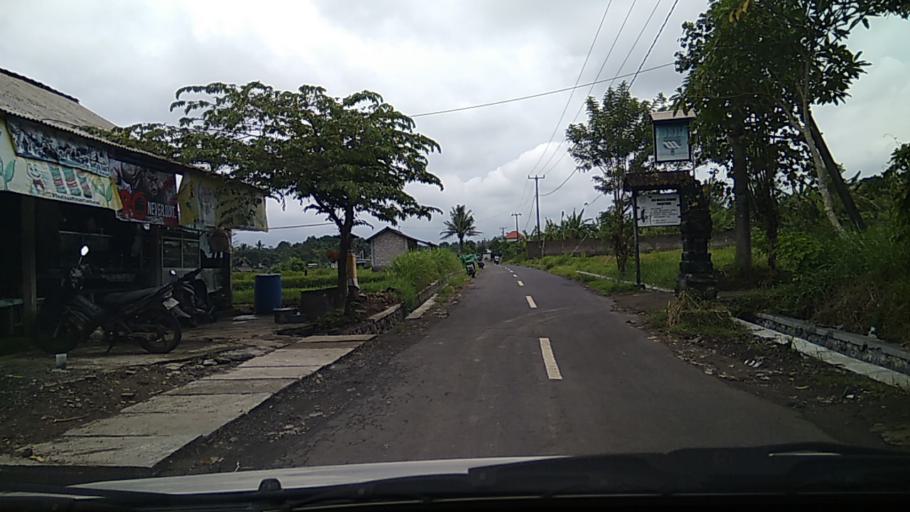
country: ID
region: Bali
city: Brahmana
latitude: -8.4768
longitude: 115.2012
